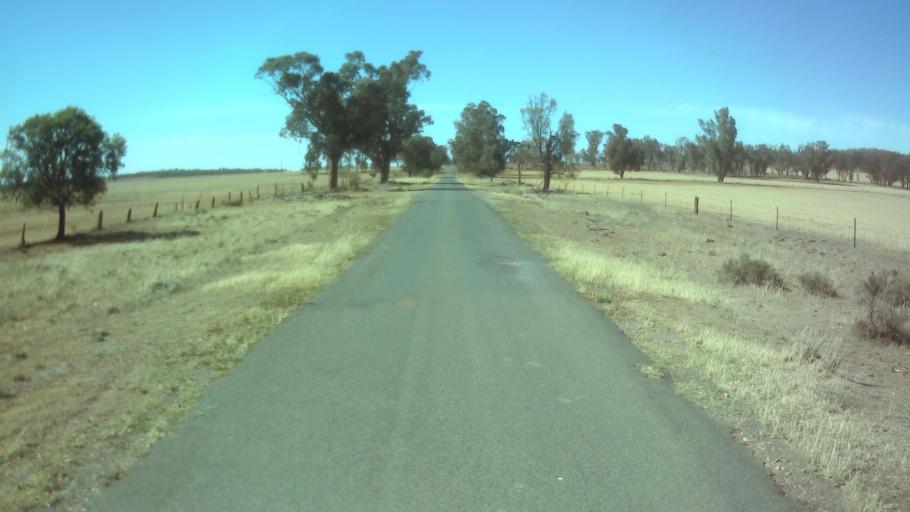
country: AU
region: New South Wales
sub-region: Forbes
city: Forbes
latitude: -33.7356
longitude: 147.7419
